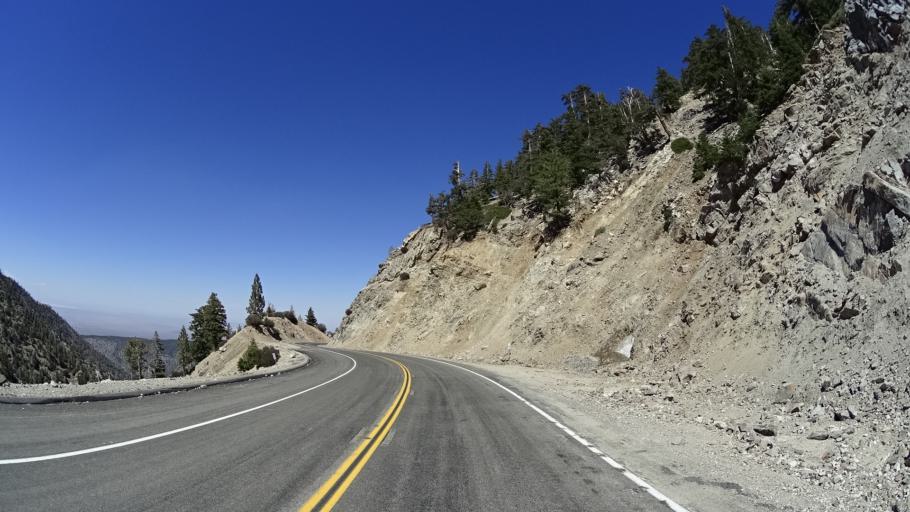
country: US
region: California
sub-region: San Bernardino County
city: Wrightwood
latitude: 34.3583
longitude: -117.7968
